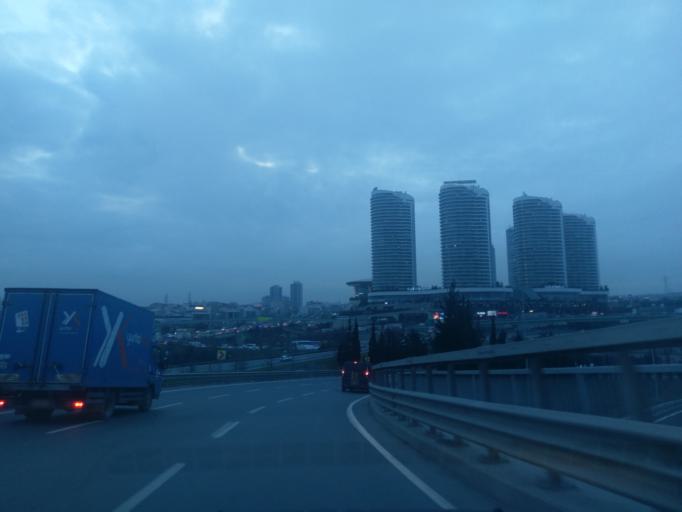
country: TR
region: Istanbul
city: Mahmutbey
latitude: 41.0625
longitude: 28.8155
